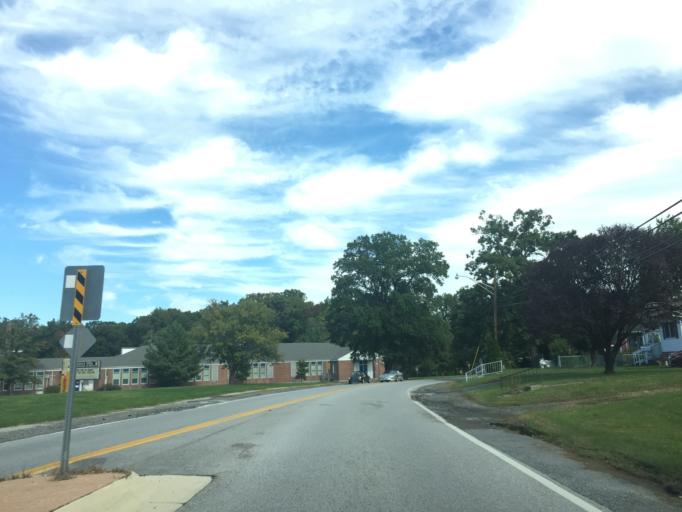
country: US
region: Maryland
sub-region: Baltimore County
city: Middle River
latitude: 39.3410
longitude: -76.4553
